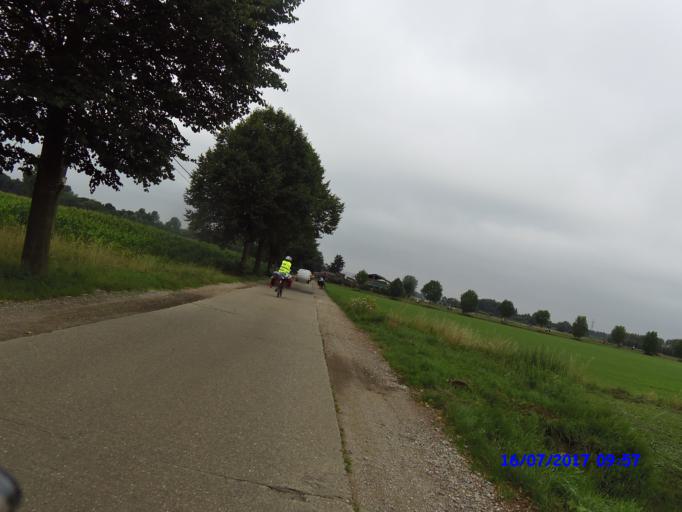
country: BE
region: Flanders
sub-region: Provincie Antwerpen
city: Lille
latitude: 51.2220
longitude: 4.8635
